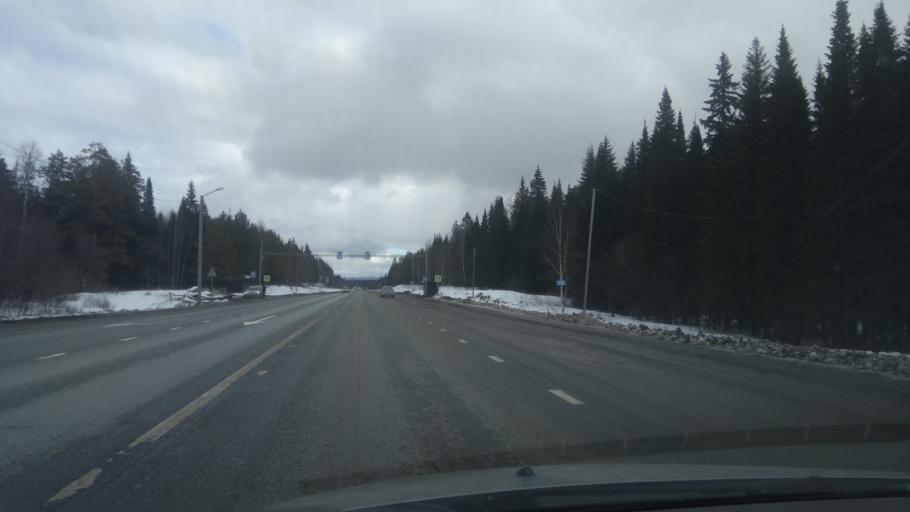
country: RU
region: Sverdlovsk
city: Druzhinino
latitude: 56.7960
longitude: 59.4149
